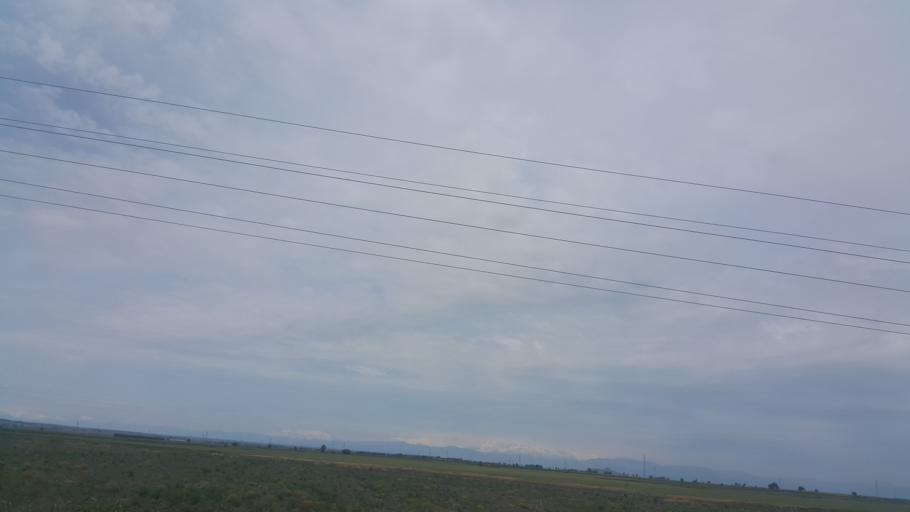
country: TR
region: Adana
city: Ceyhan
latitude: 37.0420
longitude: 35.7591
